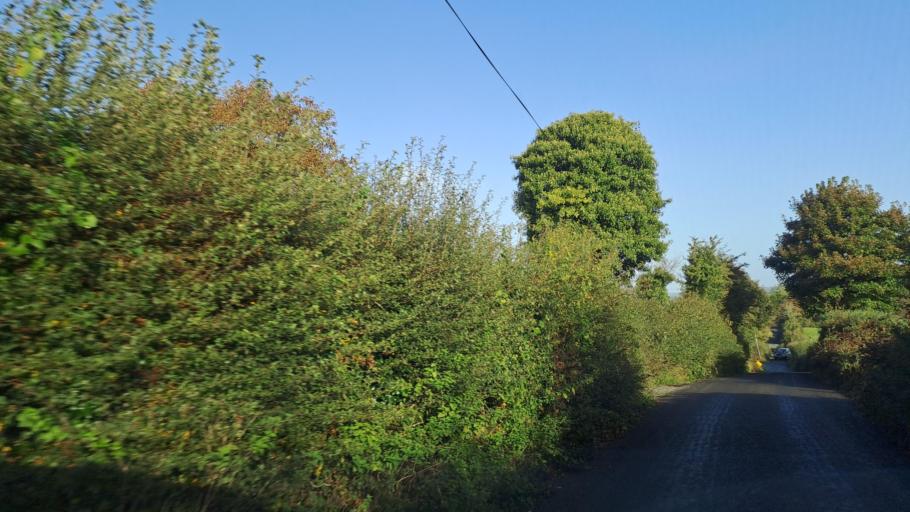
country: IE
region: Ulster
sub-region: County Monaghan
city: Castleblayney
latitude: 54.1048
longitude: -6.8918
